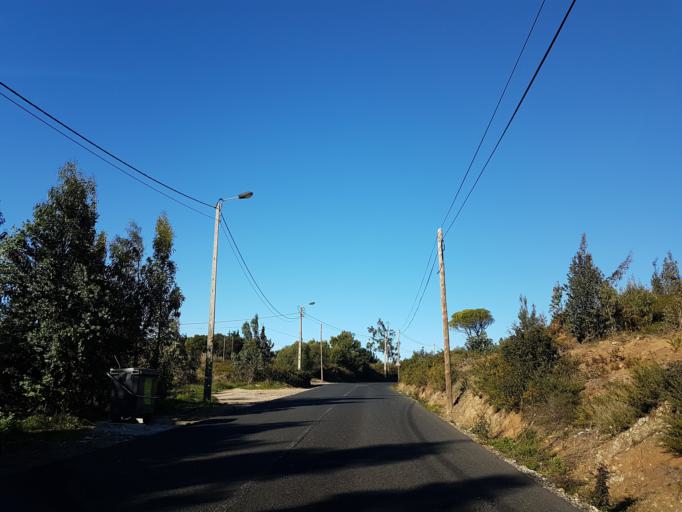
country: PT
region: Lisbon
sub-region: Cascais
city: Alcabideche
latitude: 38.7494
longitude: -9.4355
